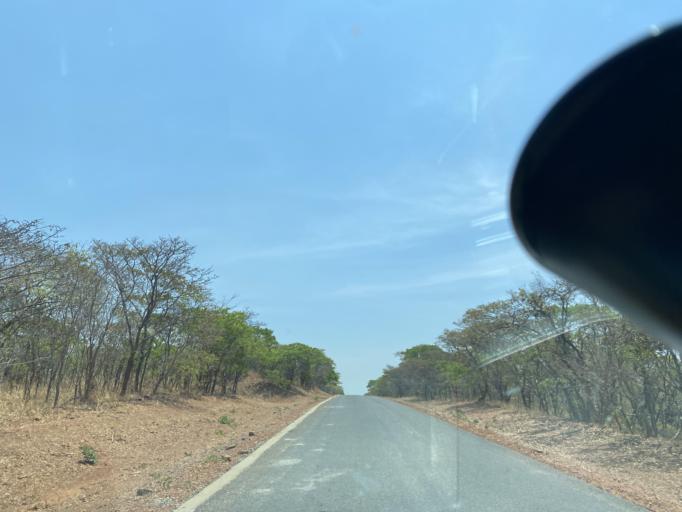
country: ZM
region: Lusaka
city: Kafue
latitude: -15.8514
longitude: 28.4174
